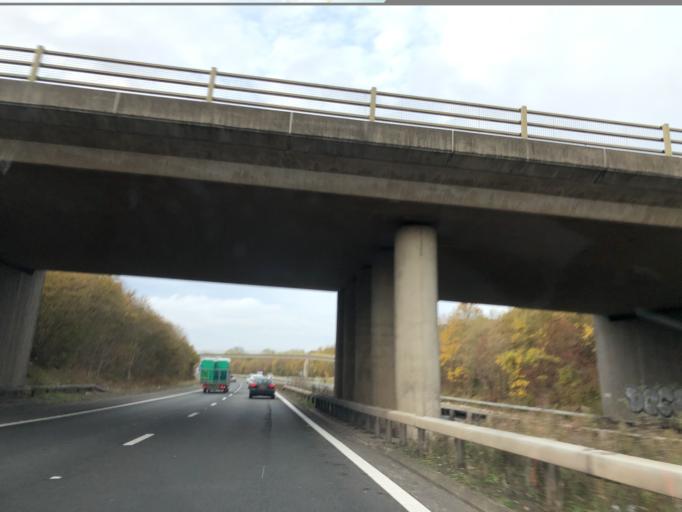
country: GB
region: England
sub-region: Royal Borough of Windsor and Maidenhead
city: White Waltham
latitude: 51.5186
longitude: -0.7644
